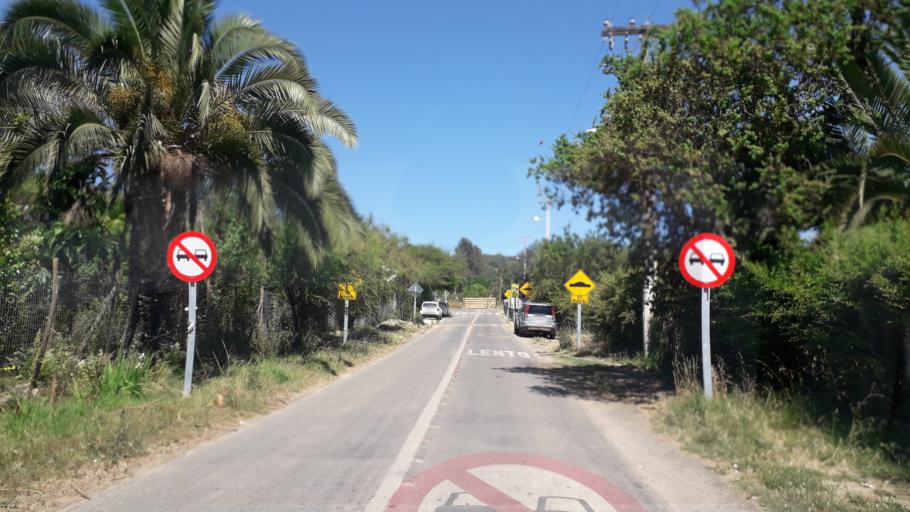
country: CL
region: Valparaiso
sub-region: Provincia de Marga Marga
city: Limache
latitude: -33.0632
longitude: -71.2230
